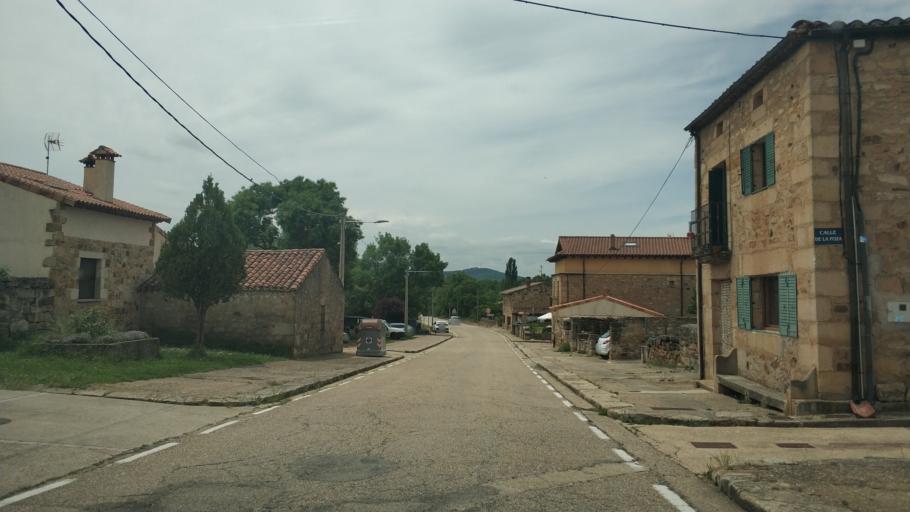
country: ES
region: Castille and Leon
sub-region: Provincia de Soria
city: Sotillo del Rincon
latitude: 41.9071
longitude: -2.6465
